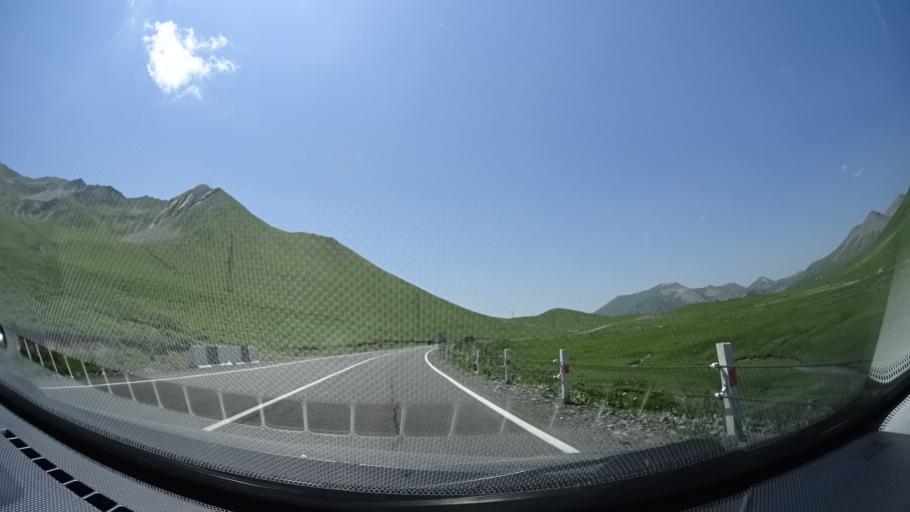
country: GE
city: Gudauri
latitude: 42.5136
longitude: 44.4624
